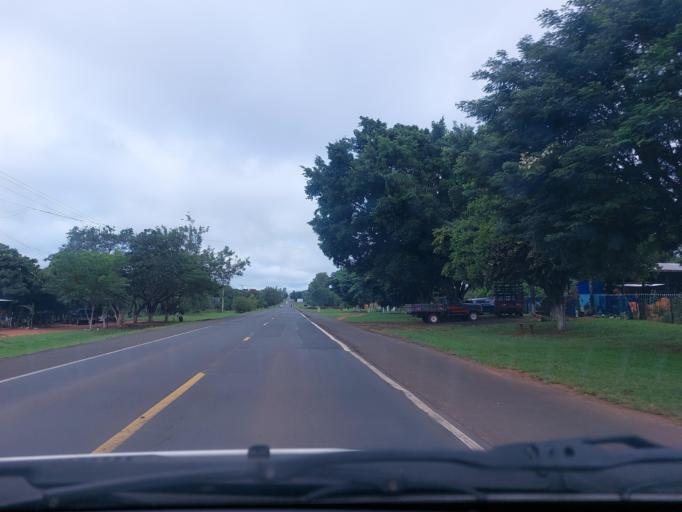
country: PY
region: San Pedro
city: Guayaybi
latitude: -24.5547
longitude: -56.4037
